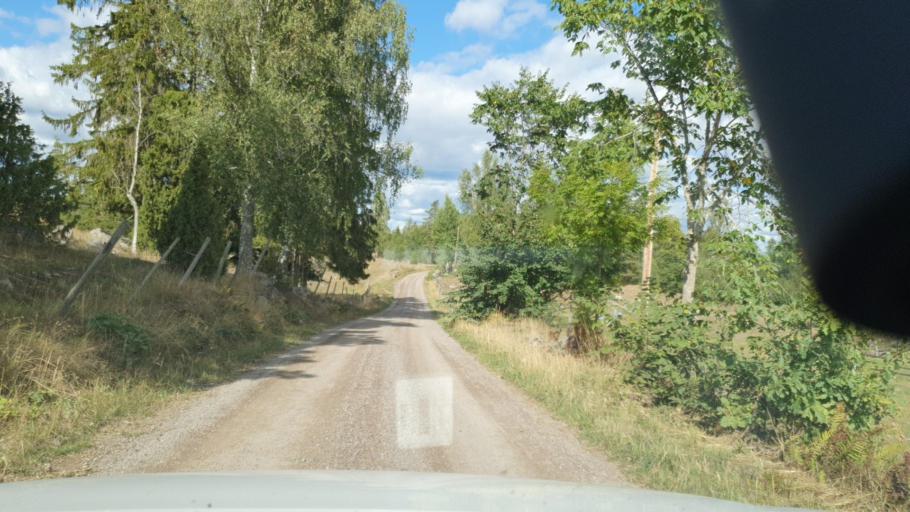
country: SE
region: Kalmar
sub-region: Hultsfreds Kommun
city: Malilla
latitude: 57.3156
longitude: 15.8135
